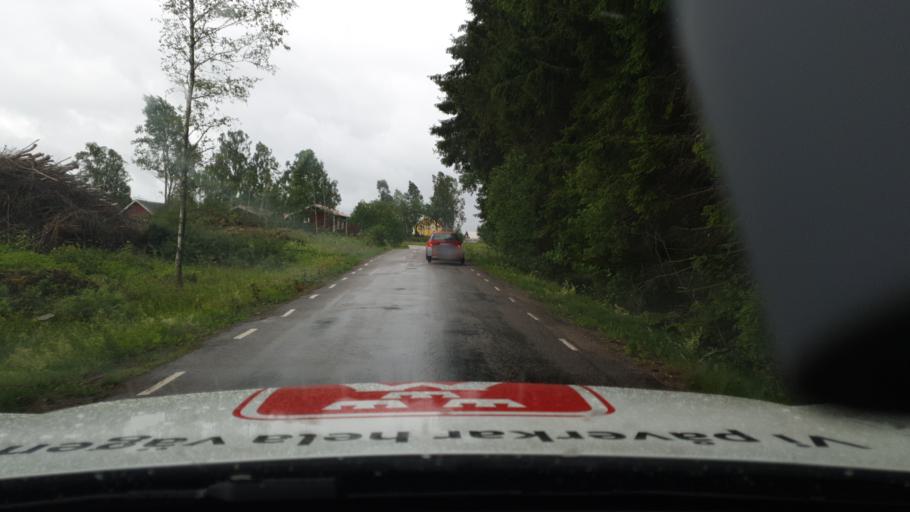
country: SE
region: Joenkoeping
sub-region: Mullsjo Kommun
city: Mullsjoe
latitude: 57.9594
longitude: 13.6542
